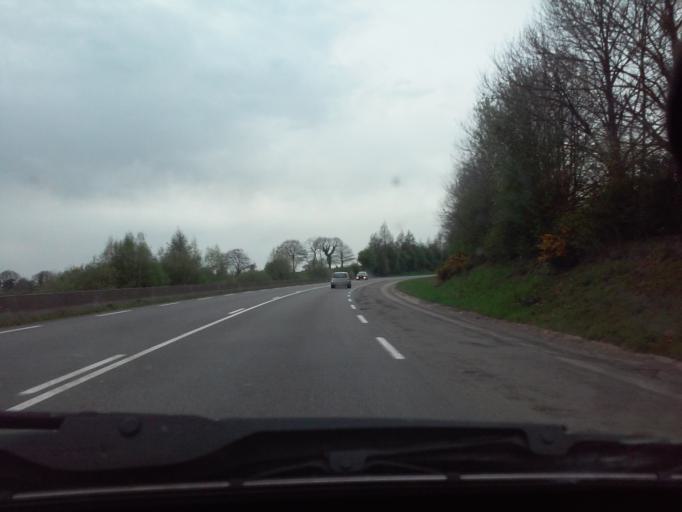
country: FR
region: Brittany
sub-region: Departement d'Ille-et-Vilaine
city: Lecousse
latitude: 48.3462
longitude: -1.2269
